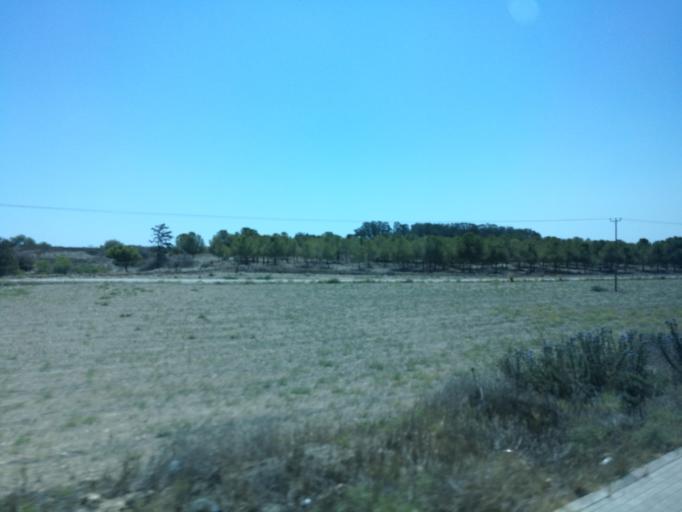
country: CY
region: Ammochostos
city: Famagusta
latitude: 35.1772
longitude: 33.8967
